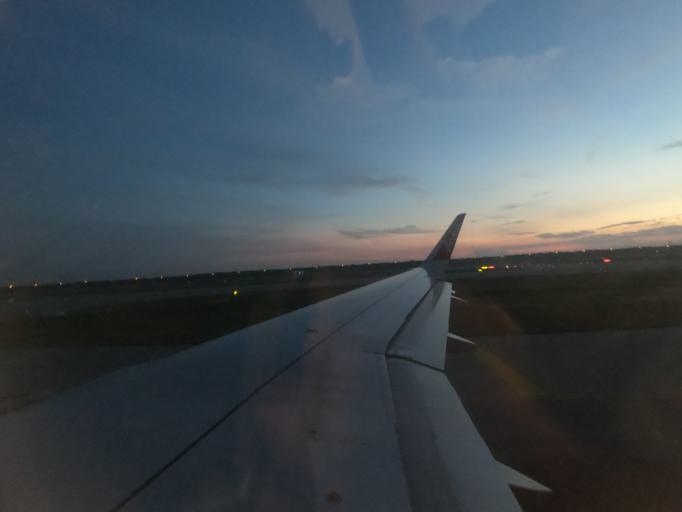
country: MY
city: Sungai Pelek New Village
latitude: 2.7346
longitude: 101.6833
